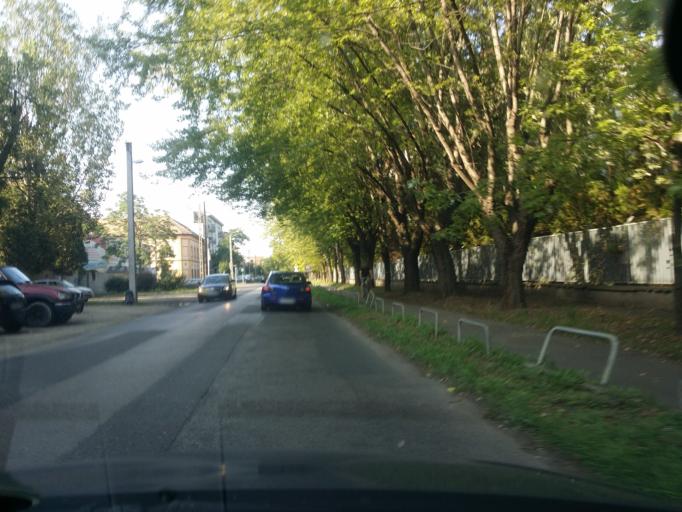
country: HU
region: Budapest
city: Budapest XIII. keruelet
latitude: 47.5272
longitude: 19.0868
